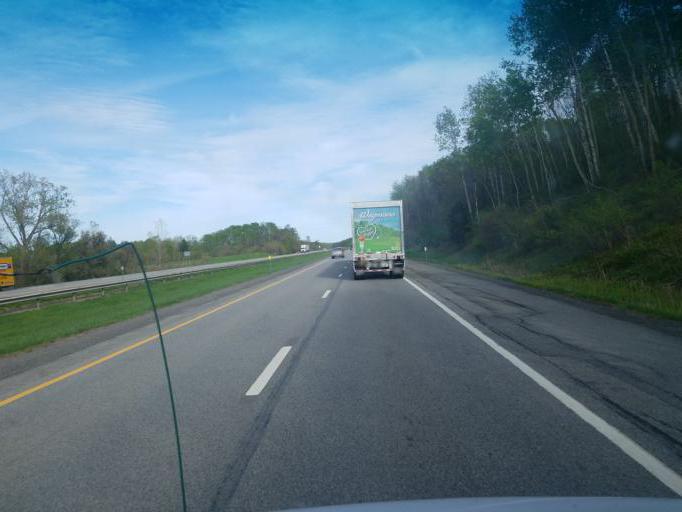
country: US
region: New York
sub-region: Herkimer County
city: Little Falls
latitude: 43.0109
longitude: -74.9164
